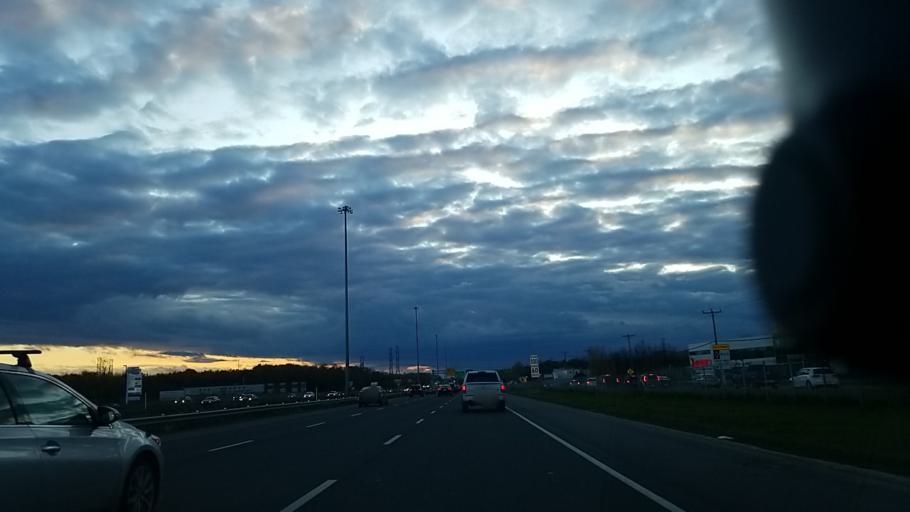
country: CA
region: Quebec
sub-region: Laurentides
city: Boisbriand
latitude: 45.5595
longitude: -73.7931
